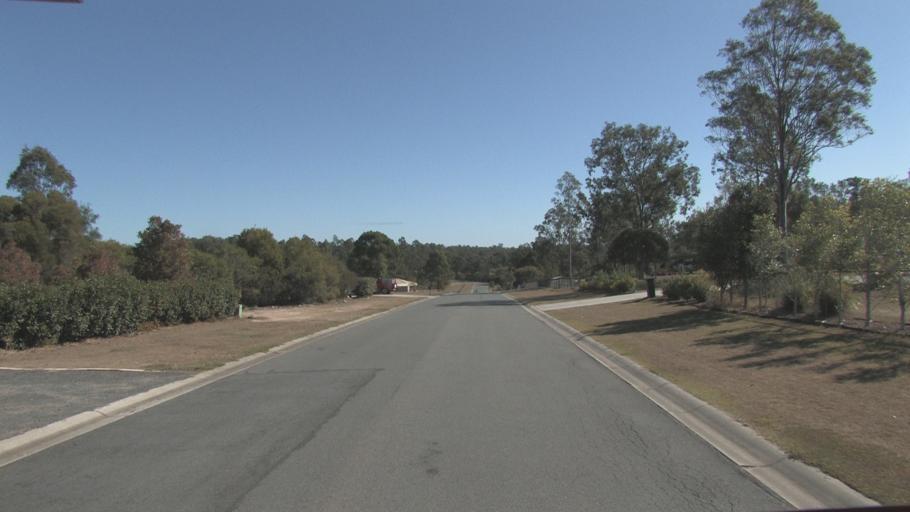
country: AU
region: Queensland
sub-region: Logan
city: Cedar Vale
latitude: -27.8580
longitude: 153.0439
